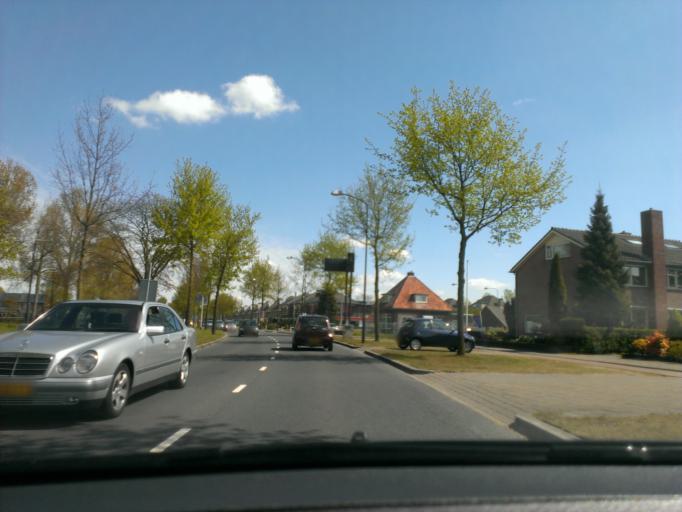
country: NL
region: Gelderland
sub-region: Gemeente Apeldoorn
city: Apeldoorn
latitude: 52.2142
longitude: 5.9875
